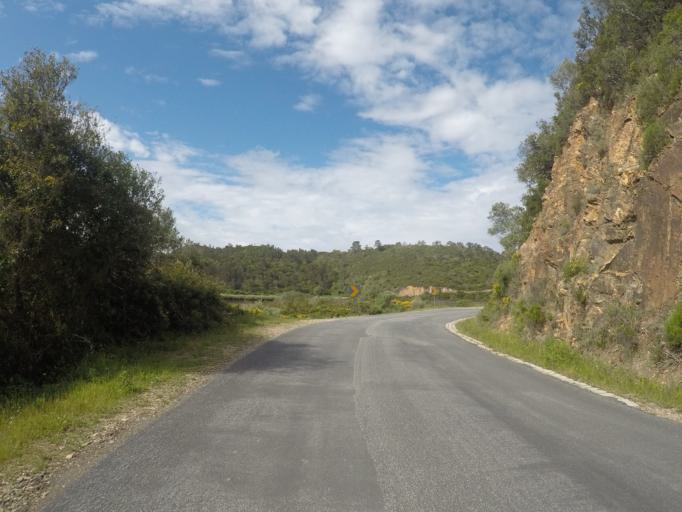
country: PT
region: Beja
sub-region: Odemira
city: Sao Teotonio
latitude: 37.4361
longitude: -8.7864
